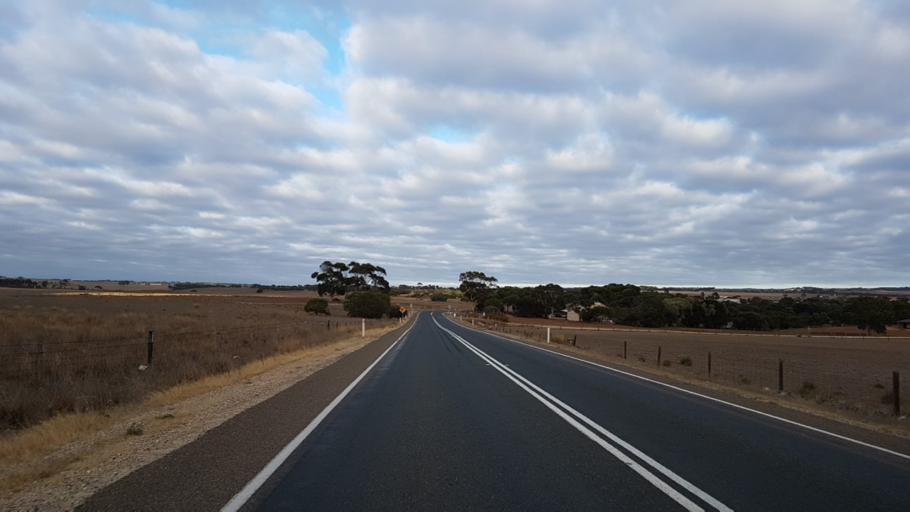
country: AU
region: South Australia
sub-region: Alexandrina
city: Strathalbyn
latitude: -35.2020
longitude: 138.9751
